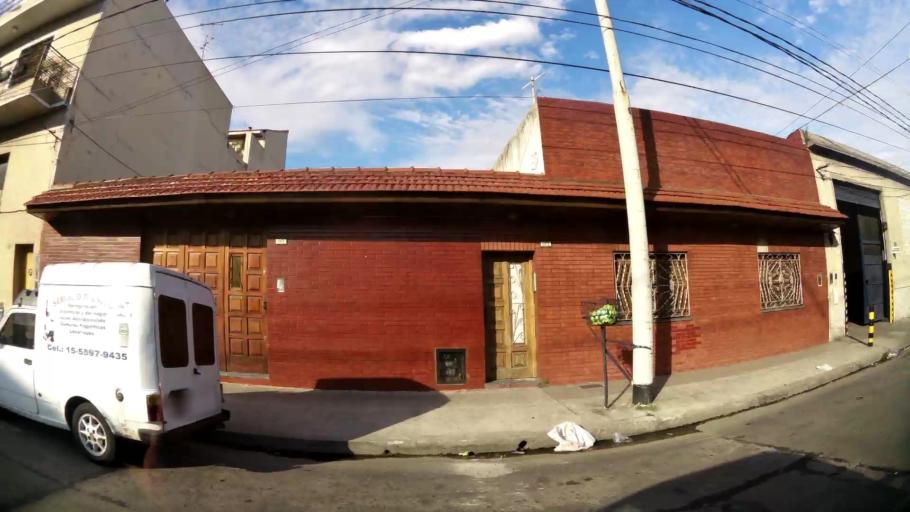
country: AR
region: Buenos Aires
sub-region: Partido de Avellaneda
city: Avellaneda
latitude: -34.6903
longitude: -58.3542
